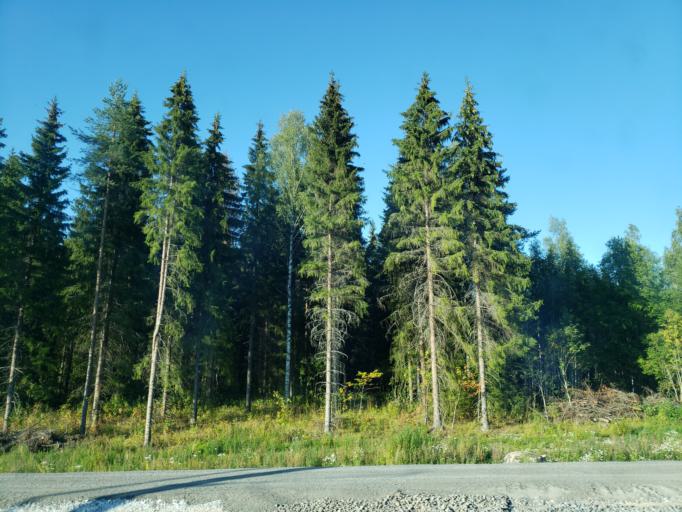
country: FI
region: South Karelia
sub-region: Lappeenranta
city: Nuijamaa
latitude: 60.8560
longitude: 28.3360
